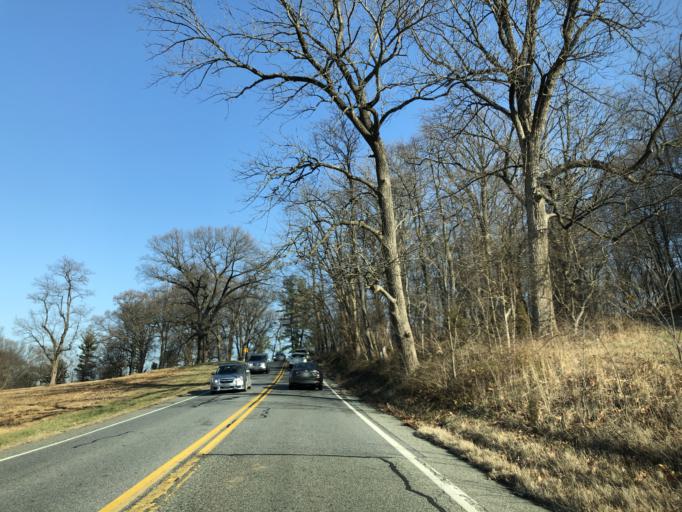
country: US
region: Pennsylvania
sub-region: Chester County
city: Chesterbrook
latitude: 40.1024
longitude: -75.4543
